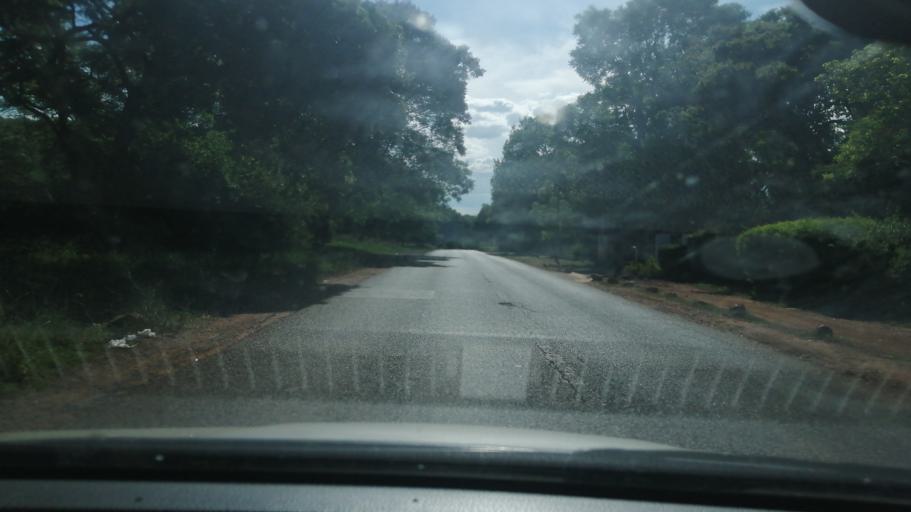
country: ZW
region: Harare
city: Harare
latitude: -17.7950
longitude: 31.0552
